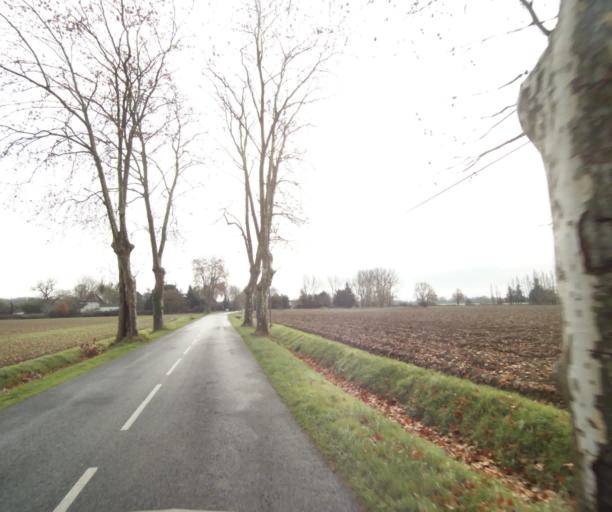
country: FR
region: Midi-Pyrenees
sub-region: Departement de la Haute-Garonne
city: Villemur-sur-Tarn
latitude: 43.8797
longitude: 1.4845
